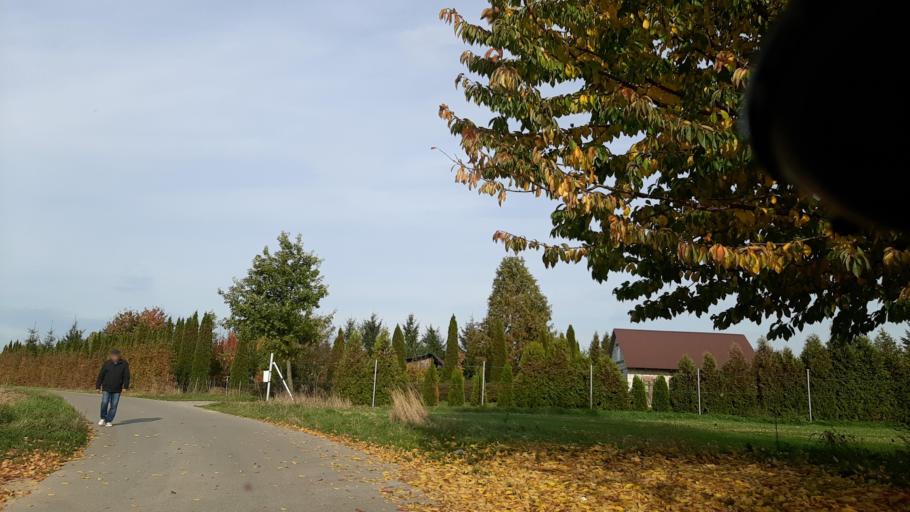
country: PL
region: Lublin Voivodeship
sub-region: Powiat lubelski
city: Jastkow
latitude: 51.3198
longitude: 22.4117
